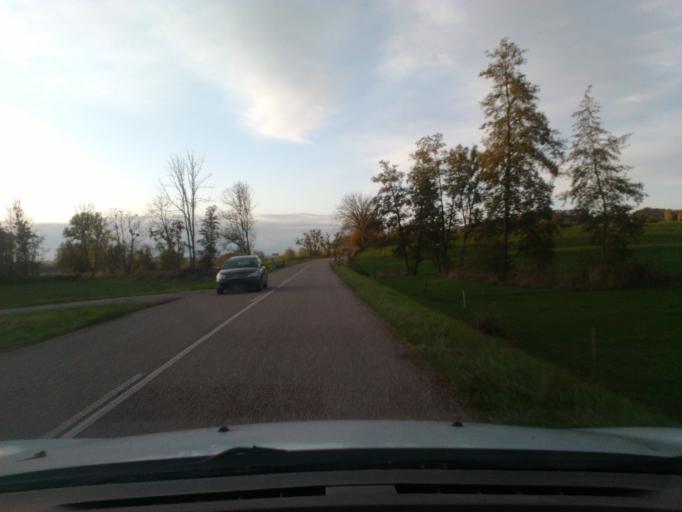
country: FR
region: Lorraine
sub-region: Departement des Vosges
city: Mirecourt
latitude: 48.2520
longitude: 6.1995
